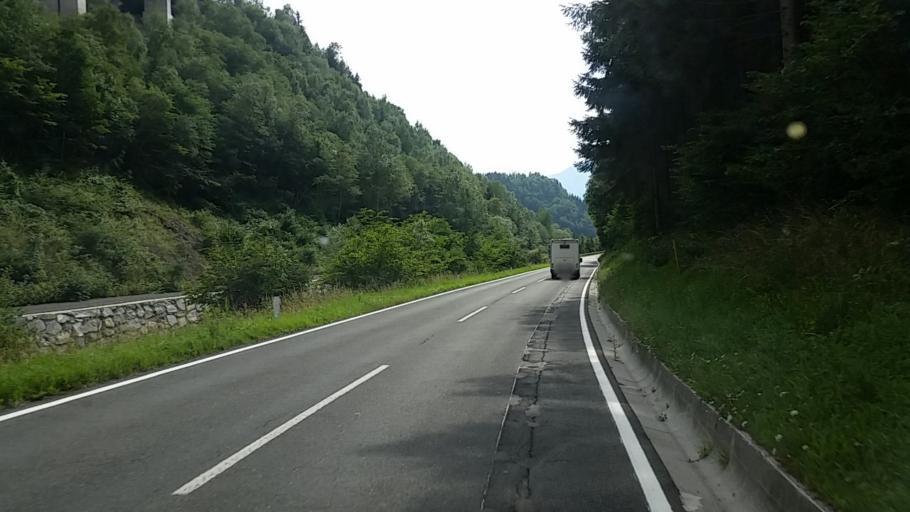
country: AT
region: Carinthia
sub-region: Politischer Bezirk Spittal an der Drau
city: Gmuend
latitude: 46.9148
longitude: 13.5595
